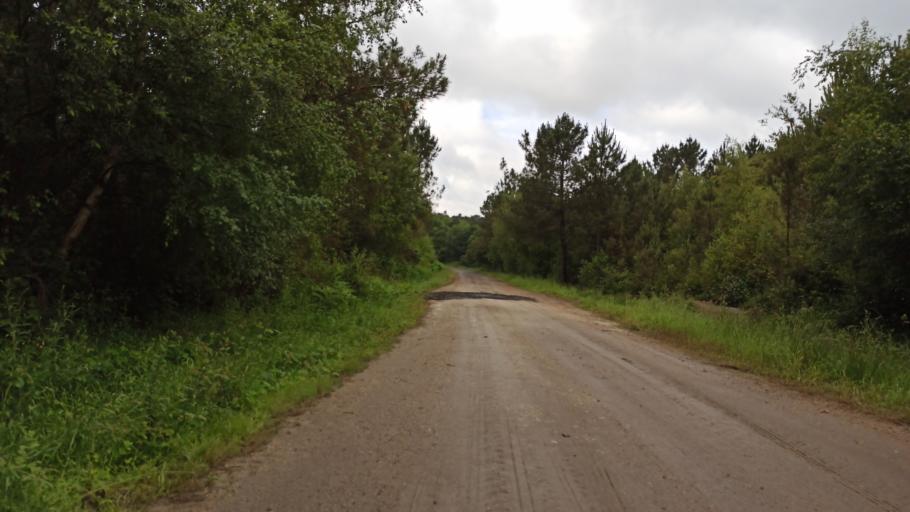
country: ES
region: Galicia
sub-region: Provincia da Coruna
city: Santiso
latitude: 42.7645
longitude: -8.0265
